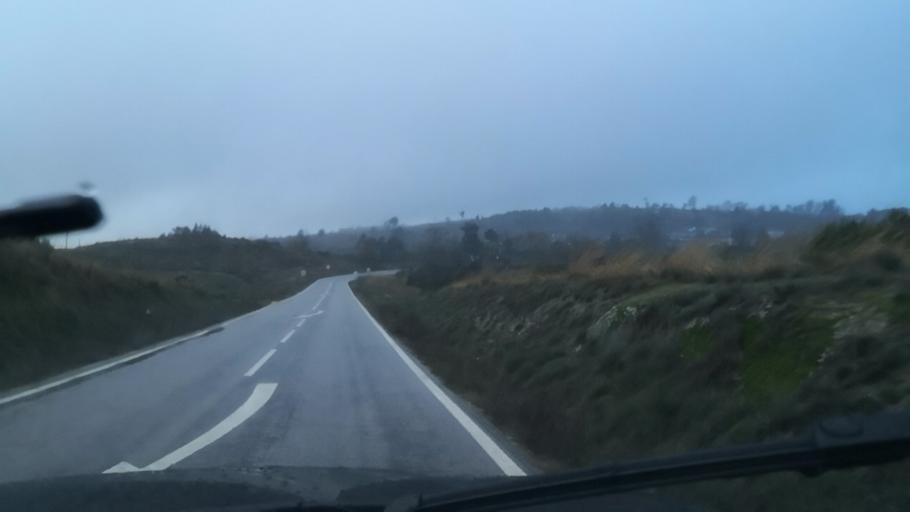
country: PT
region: Vila Real
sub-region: Vila Pouca de Aguiar
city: Vila Pouca de Aguiar
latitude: 41.4371
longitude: -7.5669
